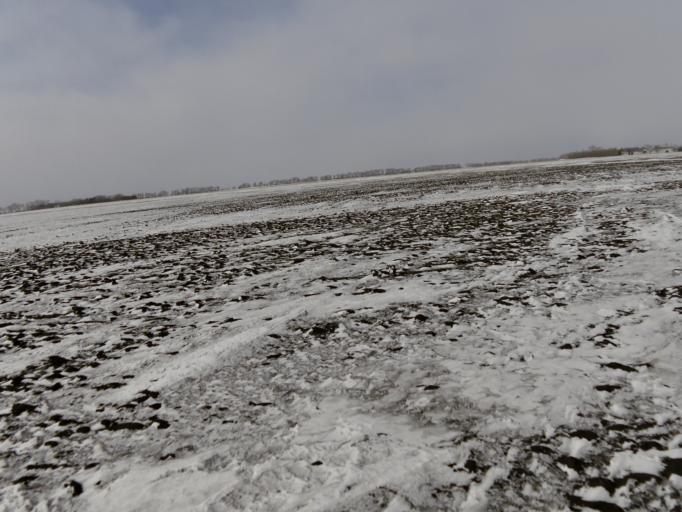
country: US
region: North Dakota
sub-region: Walsh County
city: Grafton
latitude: 48.4004
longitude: -97.2088
